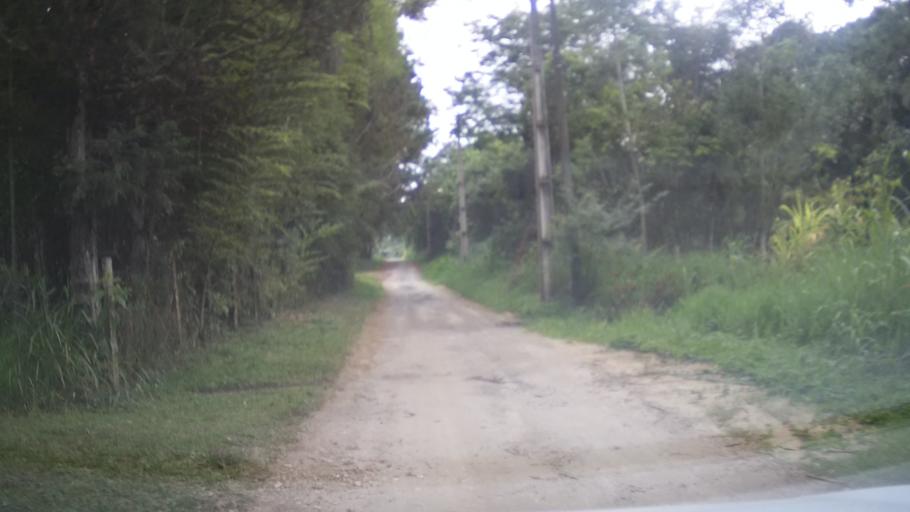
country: BR
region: Sao Paulo
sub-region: Aruja
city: Aruja
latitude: -23.3617
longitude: -46.3624
